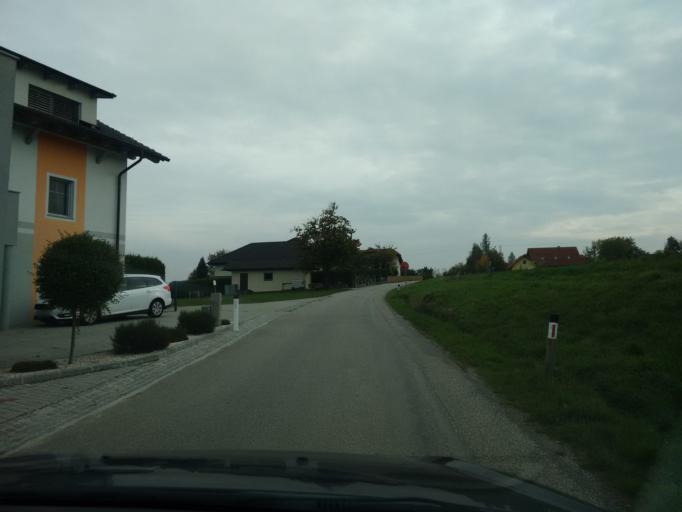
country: AT
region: Upper Austria
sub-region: Wels-Land
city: Offenhausen
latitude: 48.1678
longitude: 13.8648
